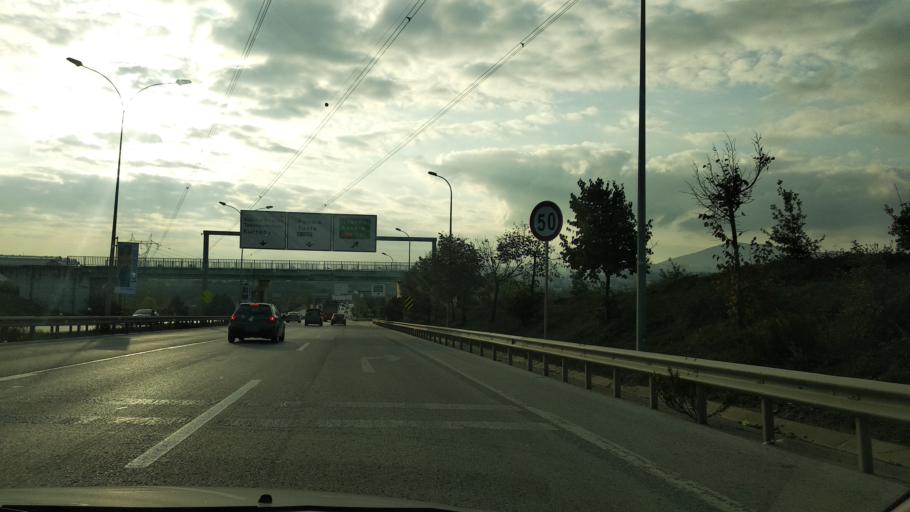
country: TR
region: Istanbul
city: Pendik
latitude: 40.9158
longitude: 29.3298
